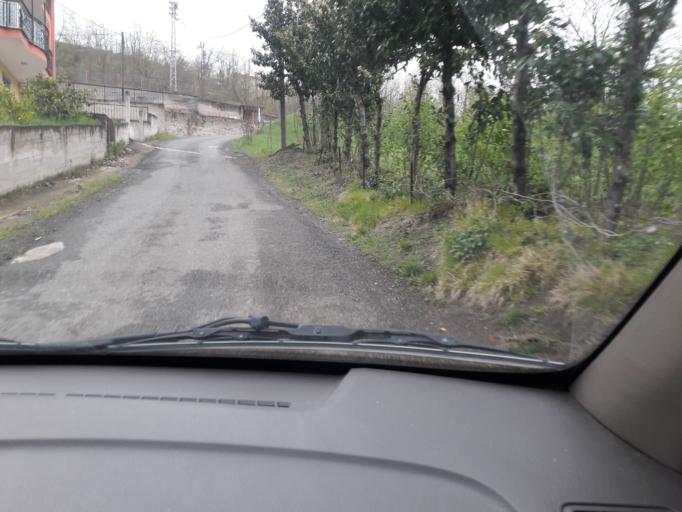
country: TR
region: Trabzon
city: Duzkoy
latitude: 40.9302
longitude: 39.4798
